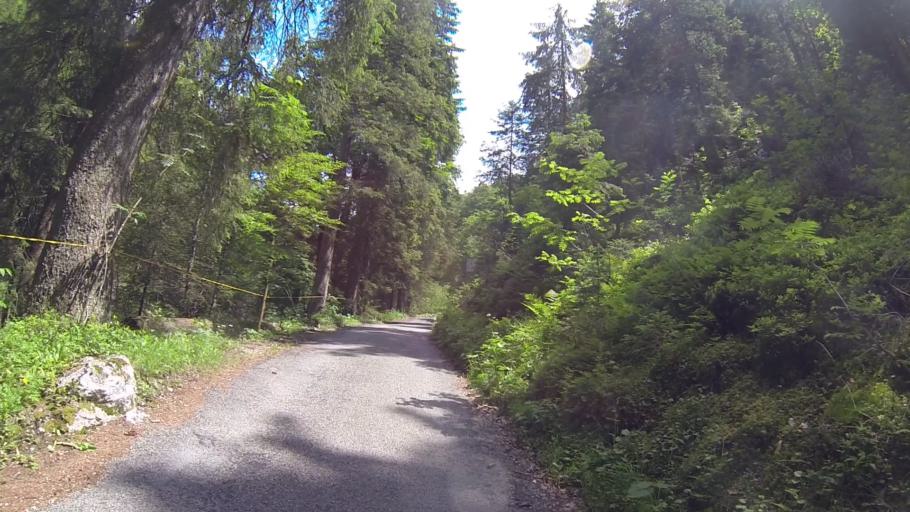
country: DE
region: Bavaria
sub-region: Swabia
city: Schwangau
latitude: 47.5336
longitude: 10.7913
